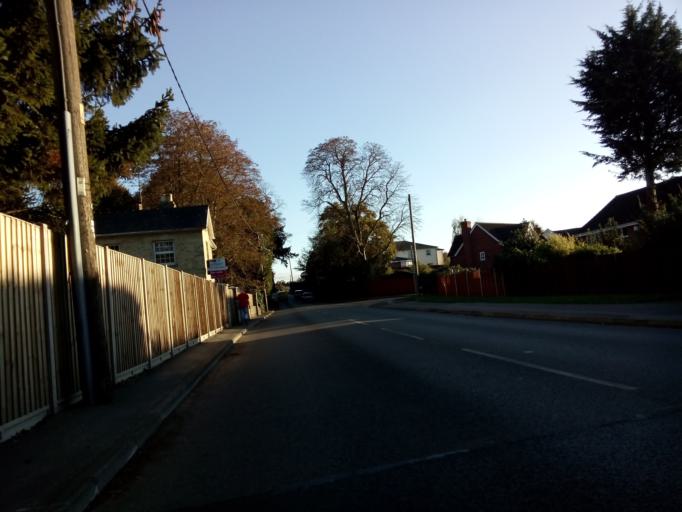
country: GB
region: England
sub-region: Suffolk
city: Sudbury
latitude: 52.0347
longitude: 0.7422
